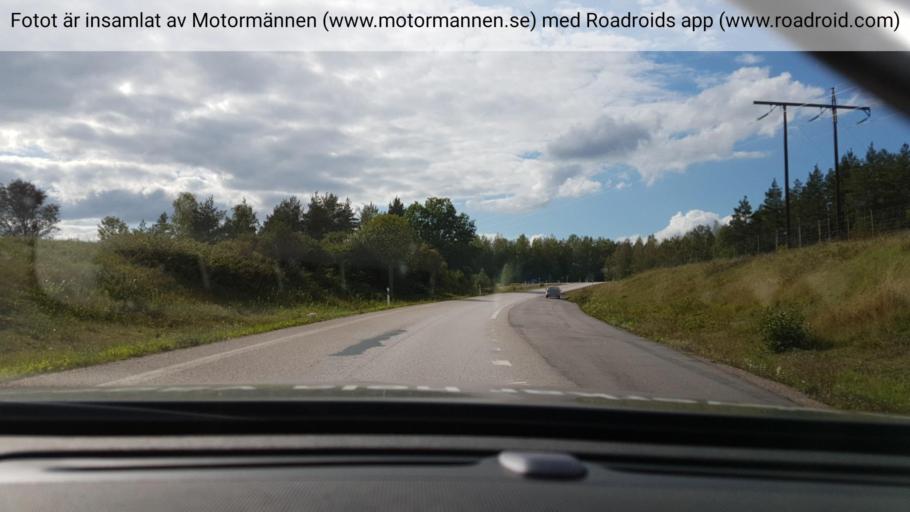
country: SE
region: OEstergoetland
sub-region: Vadstena Kommun
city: Herrestad
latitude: 58.2965
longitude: 14.9283
